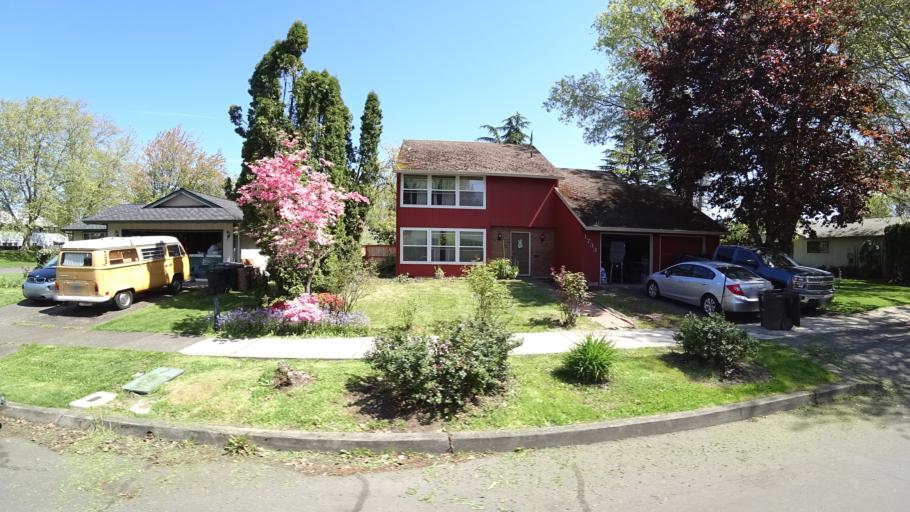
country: US
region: Oregon
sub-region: Washington County
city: Hillsboro
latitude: 45.5007
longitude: -122.9645
